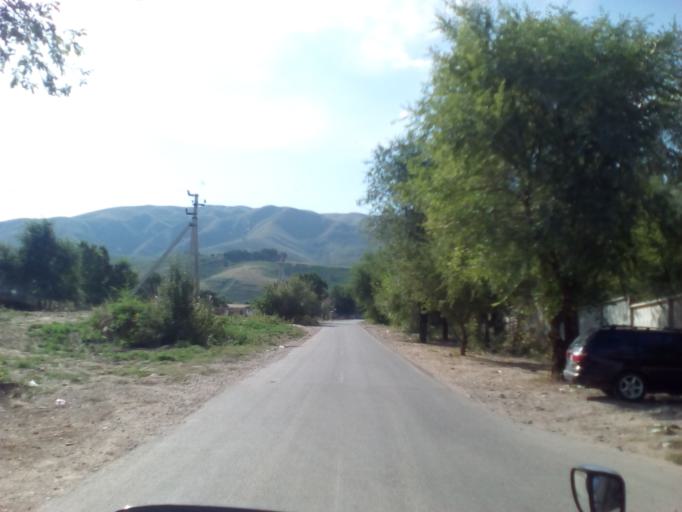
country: KZ
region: Almaty Oblysy
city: Burunday
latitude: 43.1596
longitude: 76.3826
